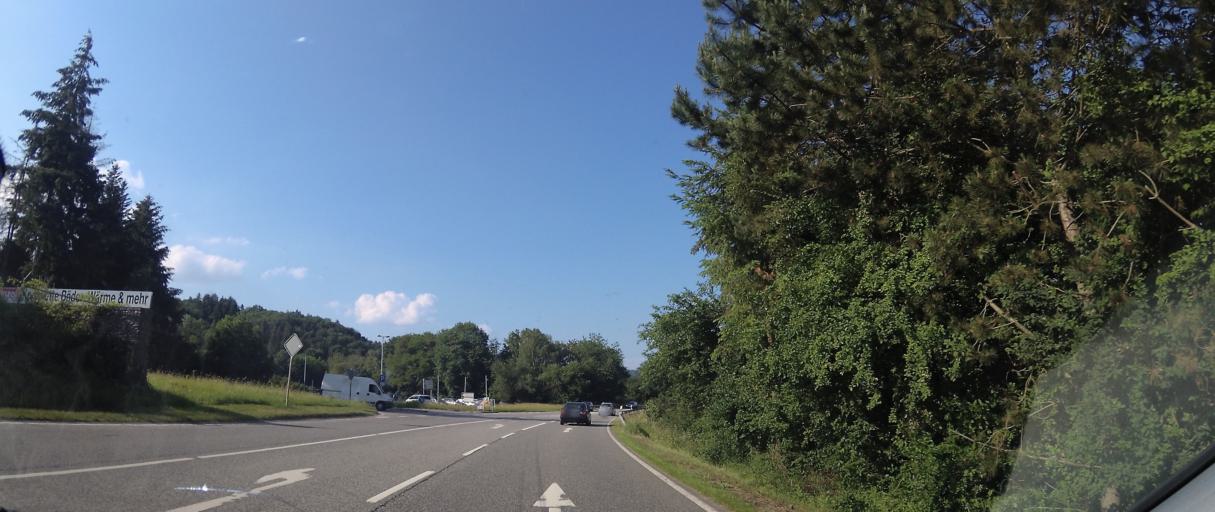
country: DE
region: Rheinland-Pfalz
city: Raumbach
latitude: 49.7128
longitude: 7.6590
